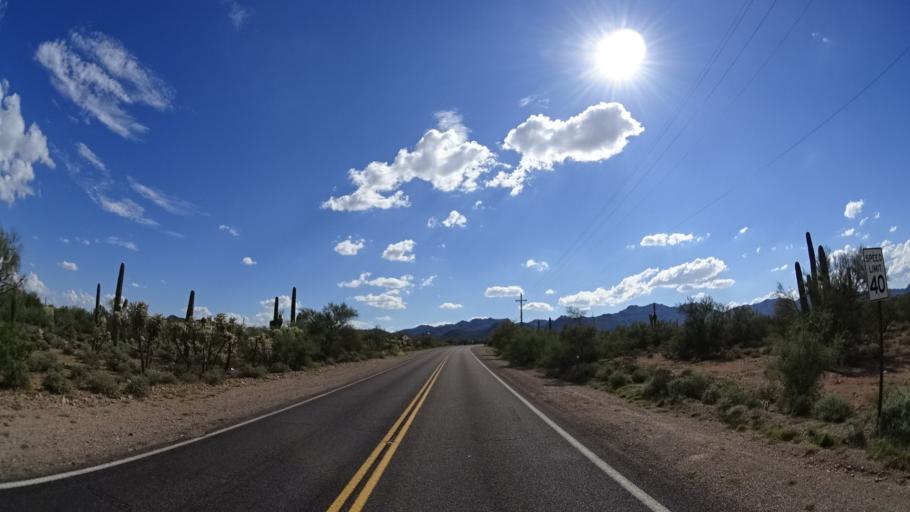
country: US
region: Arizona
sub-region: Pima County
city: Flowing Wells
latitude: 32.2791
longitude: -111.0559
